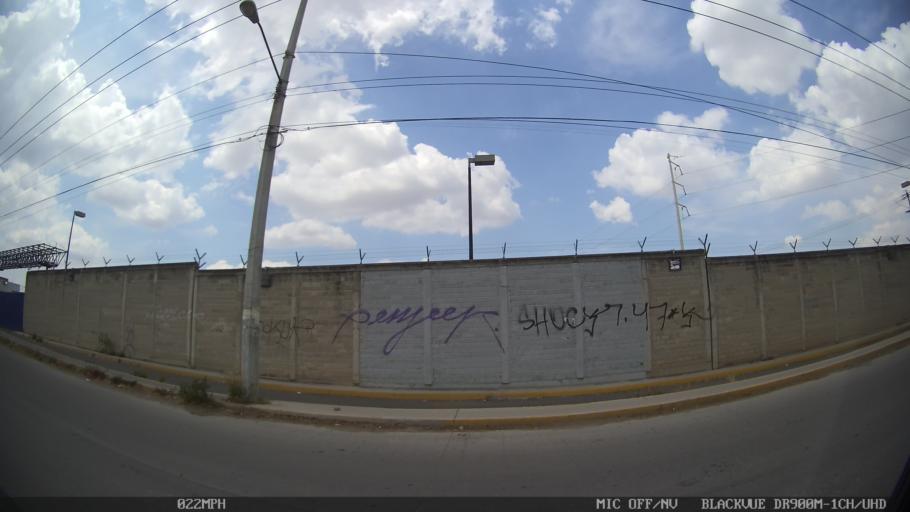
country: MX
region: Jalisco
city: Tonala
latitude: 20.6760
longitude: -103.2372
